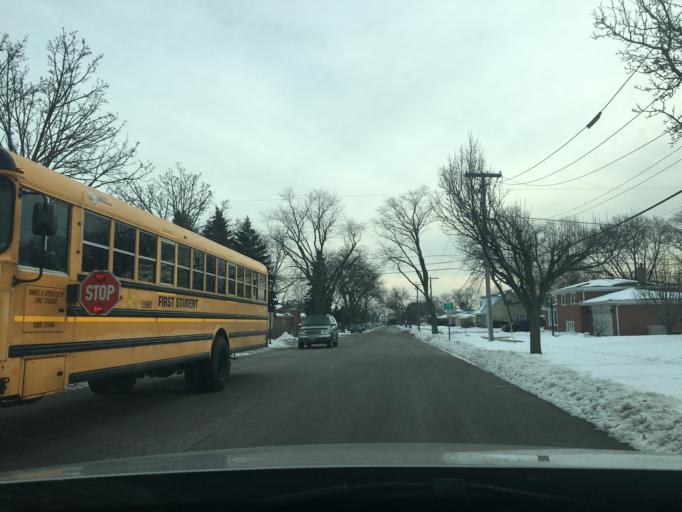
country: US
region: Illinois
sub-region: Cook County
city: Rosemont
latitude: 42.0131
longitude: -87.8941
